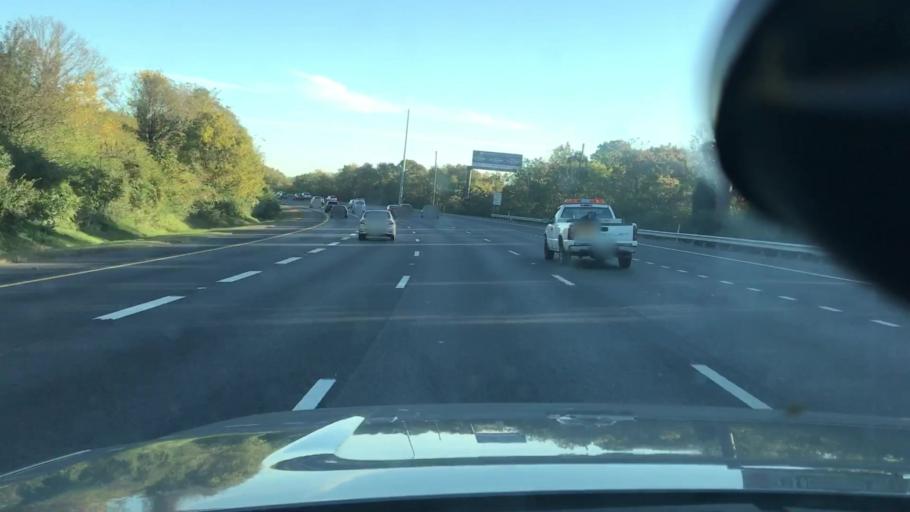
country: US
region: Tennessee
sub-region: Williamson County
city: Brentwood
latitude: 36.0459
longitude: -86.7763
